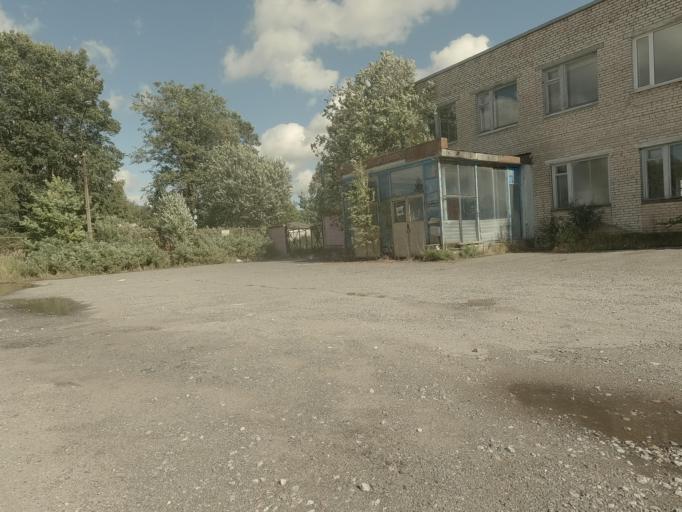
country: RU
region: Leningrad
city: Yanino Vtoroye
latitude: 59.9822
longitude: 30.5835
